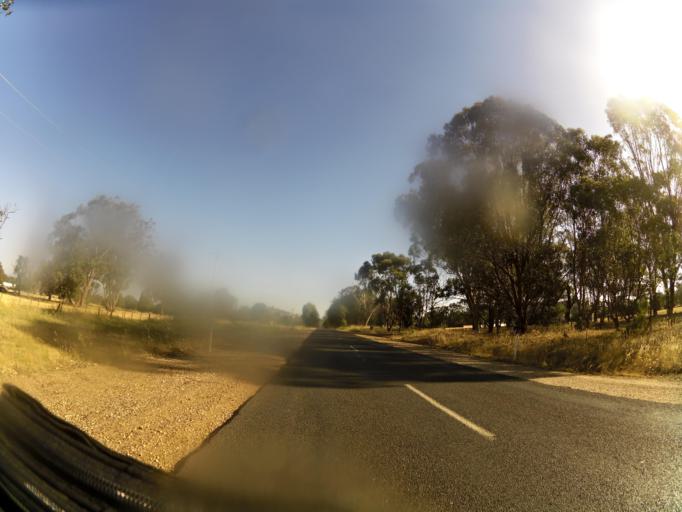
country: AU
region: Victoria
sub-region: Murrindindi
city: Kinglake West
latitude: -36.9923
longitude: 145.1125
